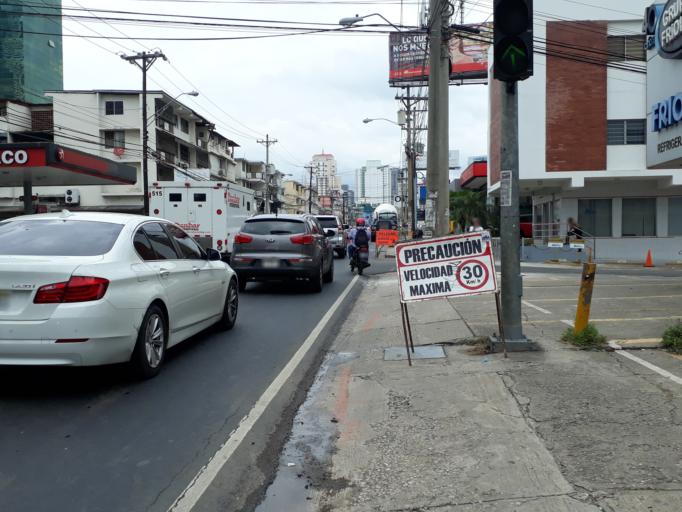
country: PA
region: Panama
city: Panama
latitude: 8.9902
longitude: -79.5170
